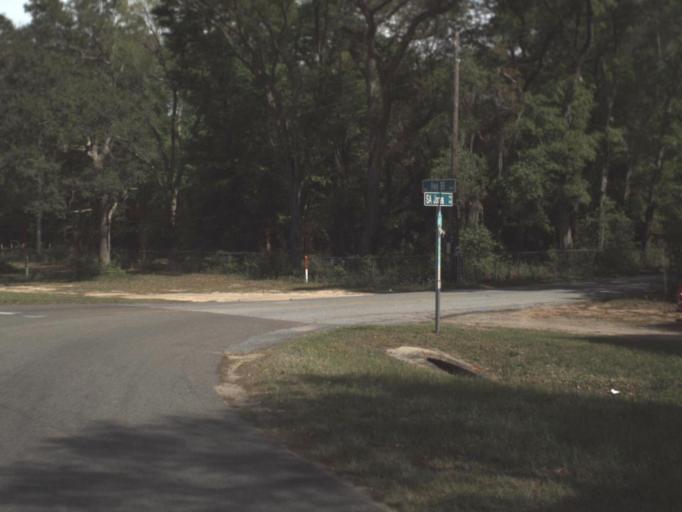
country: US
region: Florida
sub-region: Santa Rosa County
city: East Milton
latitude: 30.6468
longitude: -86.9202
